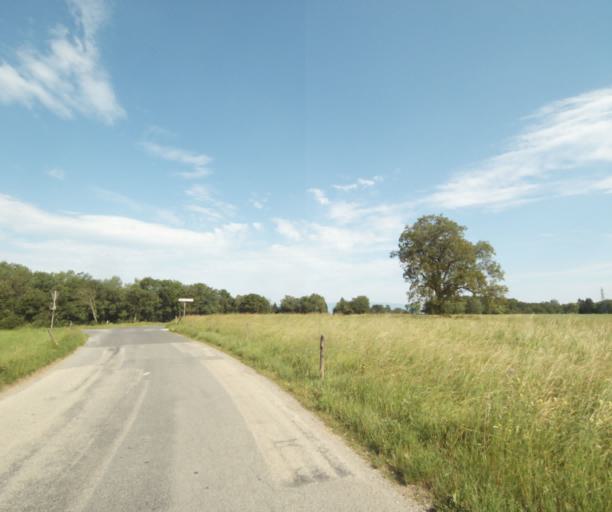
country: FR
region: Rhone-Alpes
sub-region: Departement de la Haute-Savoie
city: Allinges
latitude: 46.3279
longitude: 6.4944
